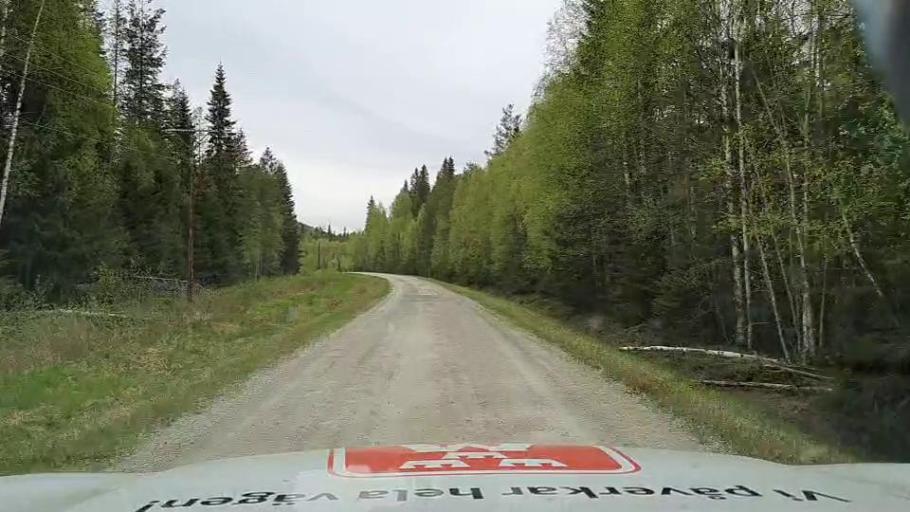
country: SE
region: Jaemtland
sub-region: Bergs Kommun
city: Hoverberg
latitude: 62.6810
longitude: 14.7982
